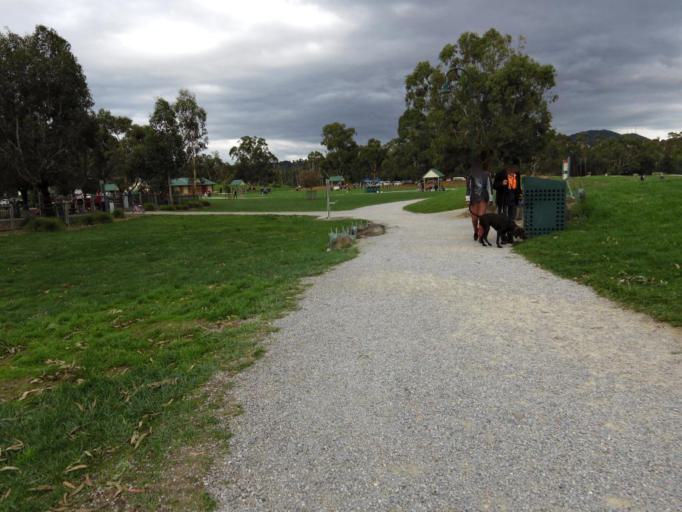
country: AU
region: Victoria
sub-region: Yarra Ranges
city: Lilydale
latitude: -37.7649
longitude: 145.3569
